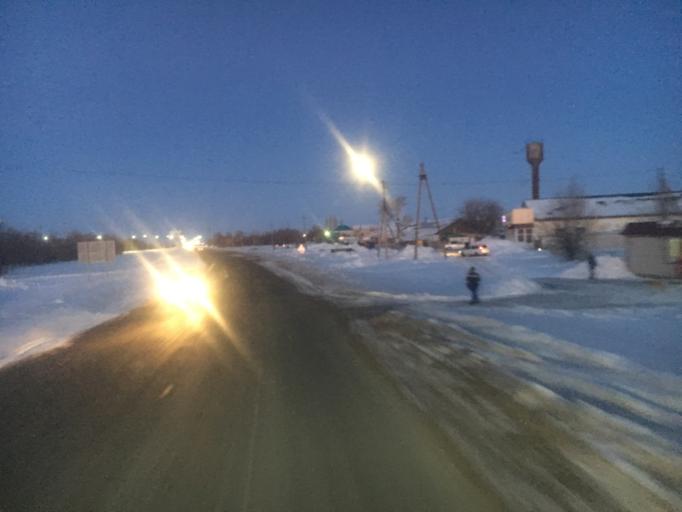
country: KZ
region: Batys Qazaqstan
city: Oral
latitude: 51.1543
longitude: 51.4899
